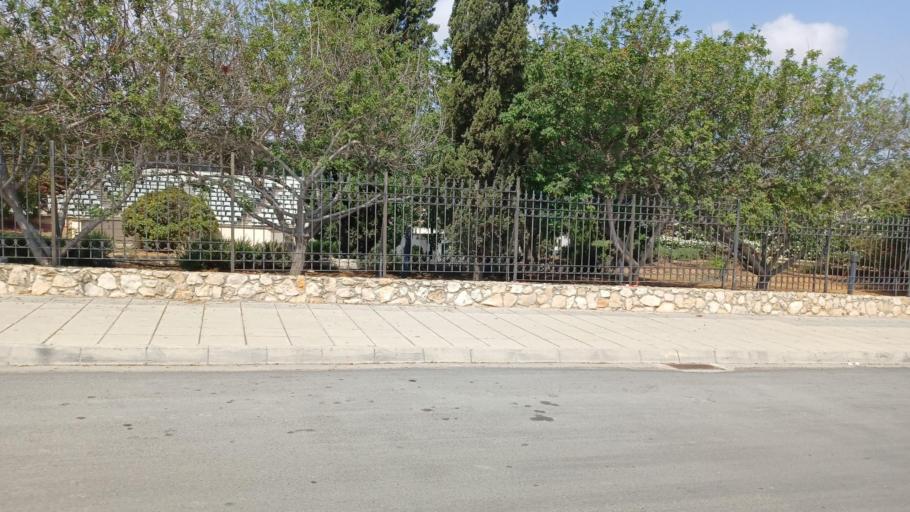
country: CY
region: Ammochostos
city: Deryneia
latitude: 35.0665
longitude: 33.9658
